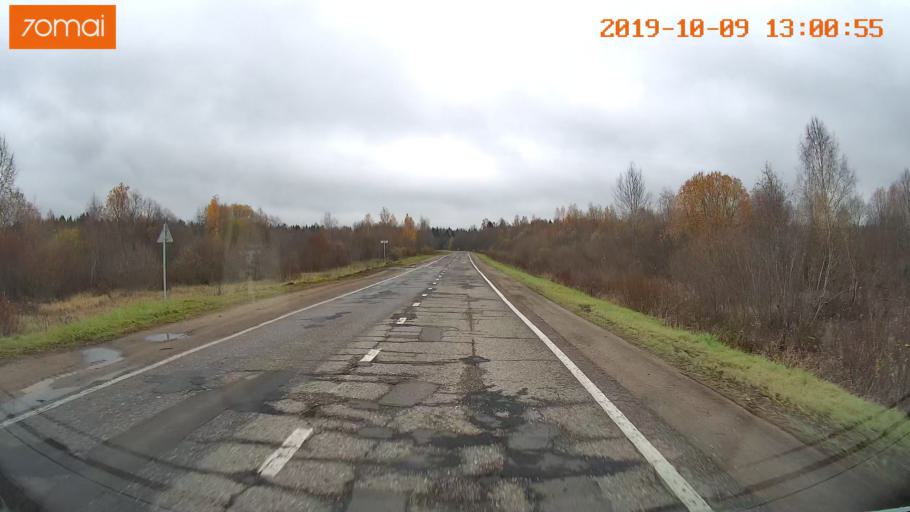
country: RU
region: Jaroslavl
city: Prechistoye
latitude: 58.3729
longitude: 40.4834
